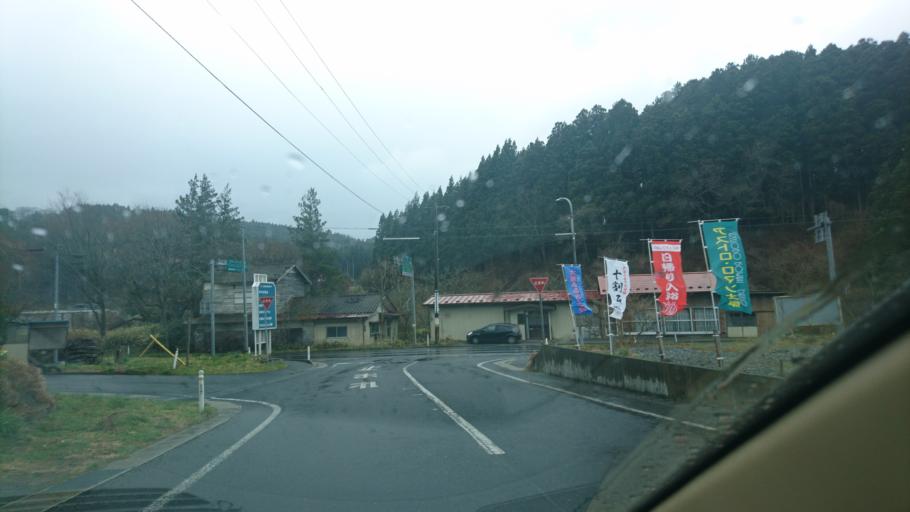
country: JP
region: Iwate
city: Ofunato
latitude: 38.9385
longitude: 141.4599
